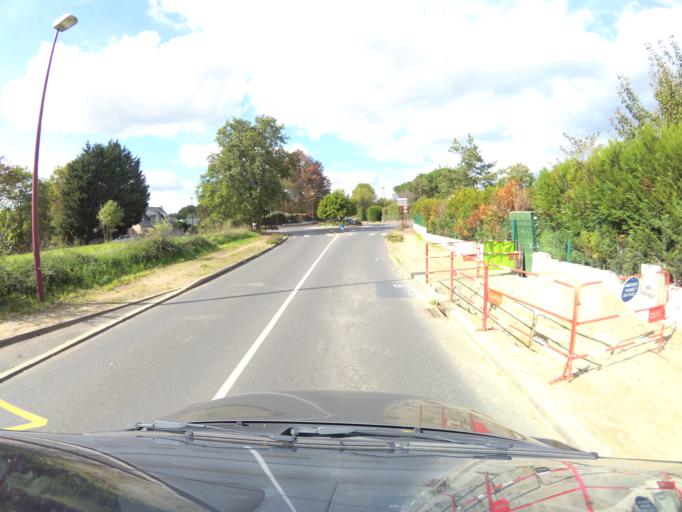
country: FR
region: Pays de la Loire
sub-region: Departement de la Loire-Atlantique
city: Suce-sur-Erdre
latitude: 47.3335
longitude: -1.5170
